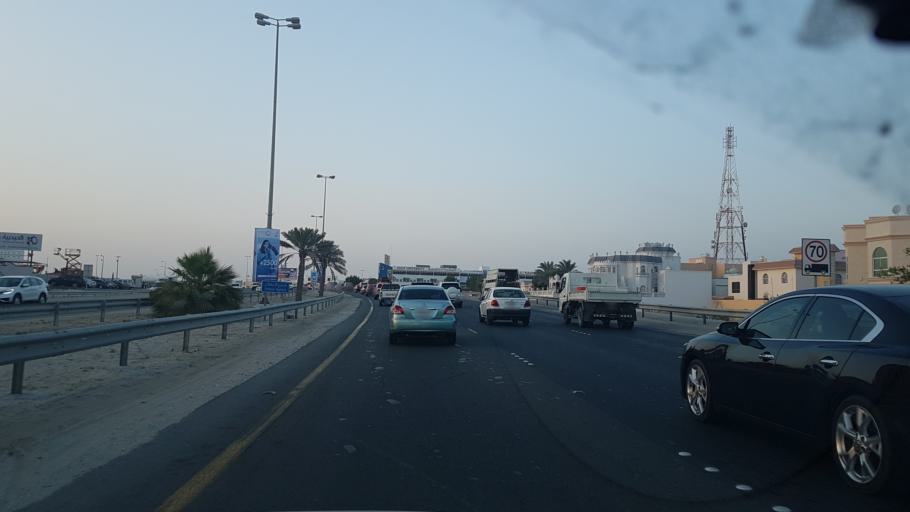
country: BH
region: Northern
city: Ar Rifa'
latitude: 26.1482
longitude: 50.5763
